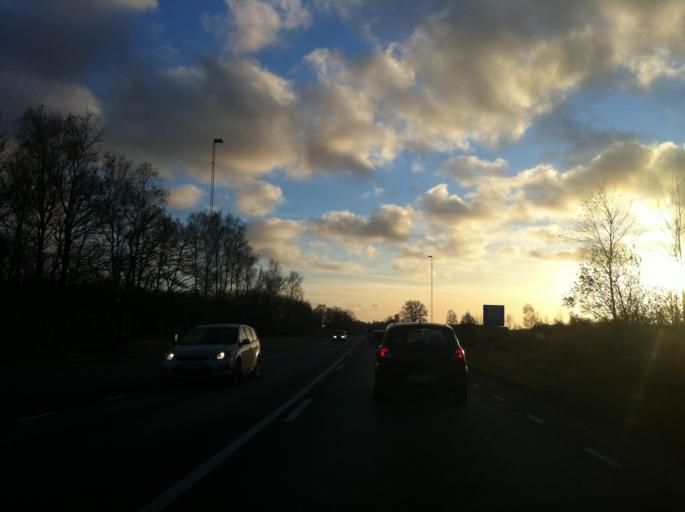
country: SE
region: Skane
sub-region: Hoors Kommun
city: Hoeoer
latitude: 55.9829
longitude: 13.6026
